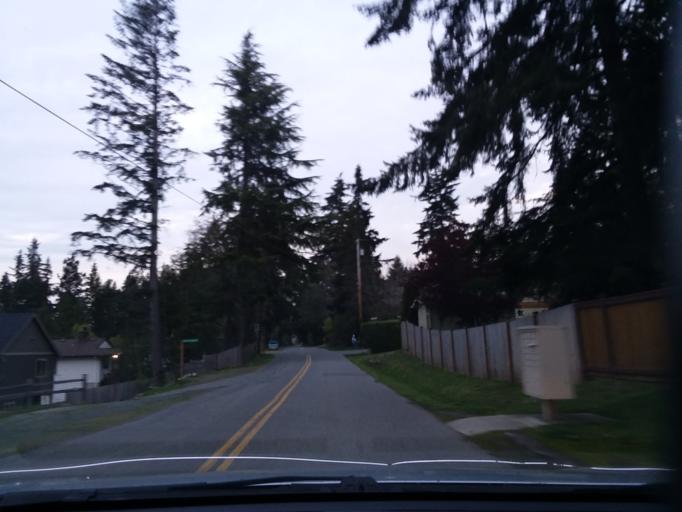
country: US
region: Washington
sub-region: Snohomish County
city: Esperance
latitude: 47.7868
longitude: -122.3515
